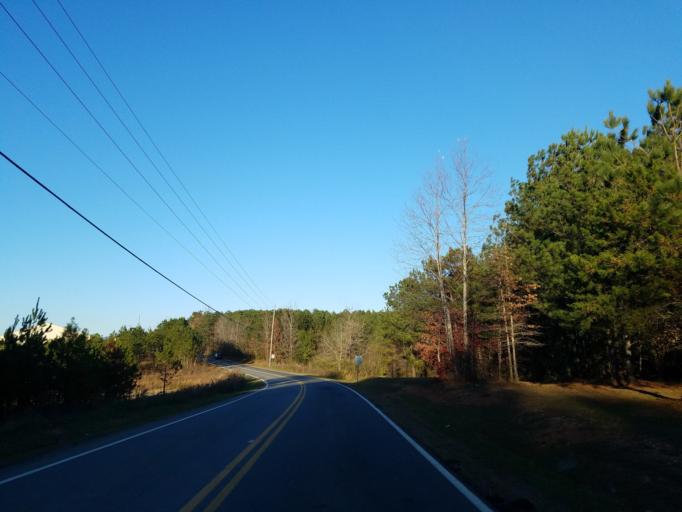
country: US
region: Georgia
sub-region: Pickens County
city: Nelson
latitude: 34.3663
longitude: -84.3709
